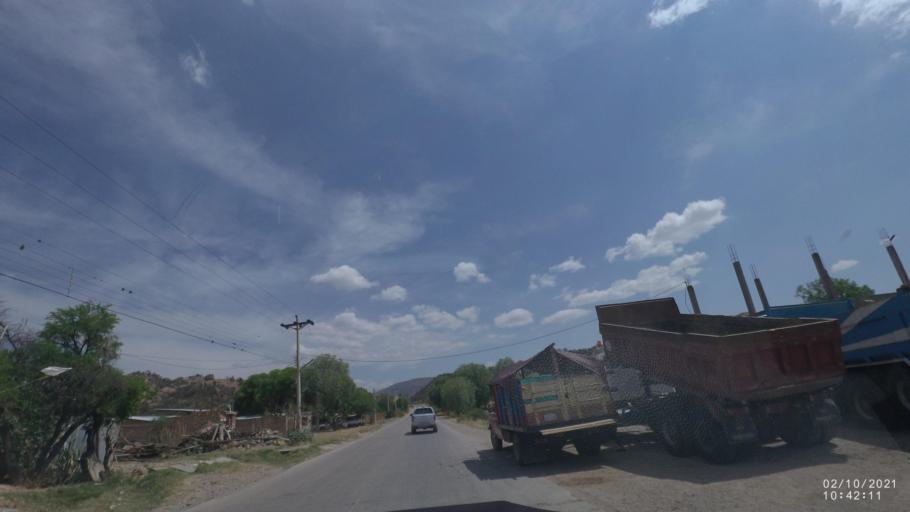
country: BO
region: Cochabamba
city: Capinota
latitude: -17.6094
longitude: -66.2933
